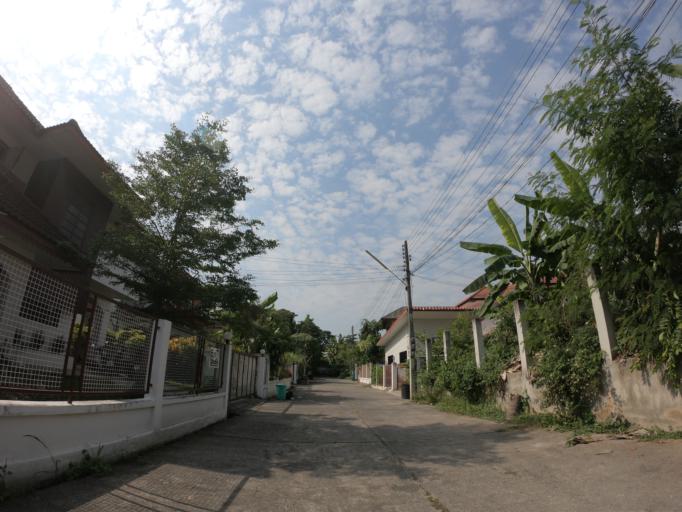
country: TH
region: Chiang Mai
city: Chiang Mai
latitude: 18.7779
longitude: 98.9588
